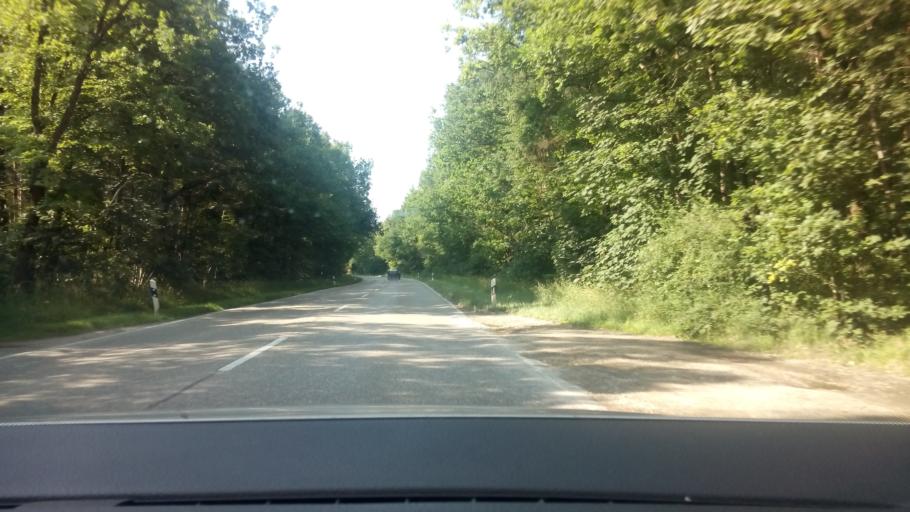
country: DE
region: Bavaria
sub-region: Upper Bavaria
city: Oberschleissheim
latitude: 48.2430
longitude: 11.5826
